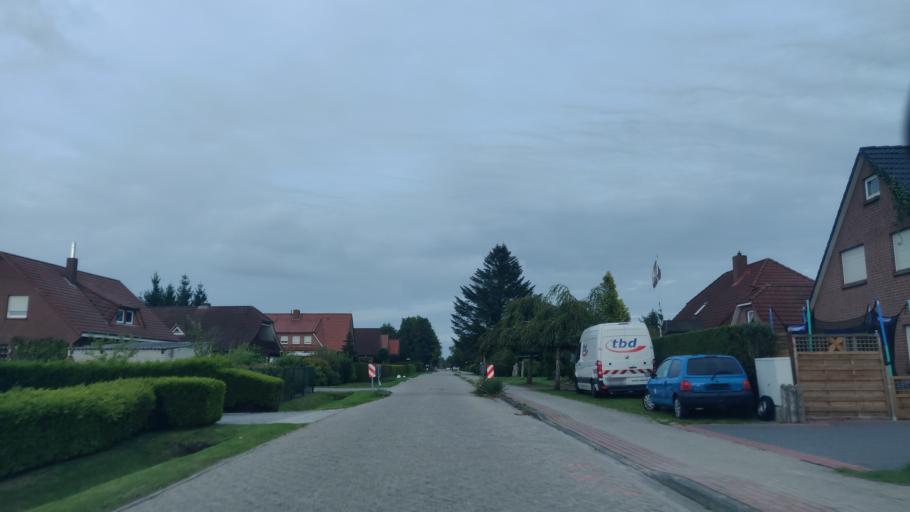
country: DE
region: Lower Saxony
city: Aurich
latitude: 53.4826
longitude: 7.4005
